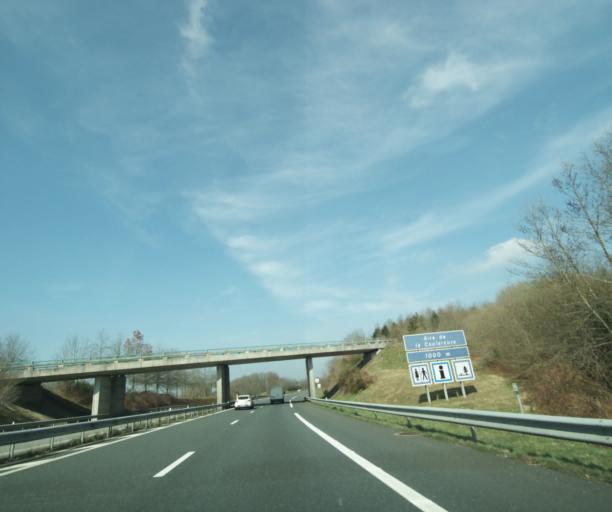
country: FR
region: Limousin
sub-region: Departement de la Haute-Vienne
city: Bessines-sur-Gartempe
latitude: 46.1414
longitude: 1.3768
